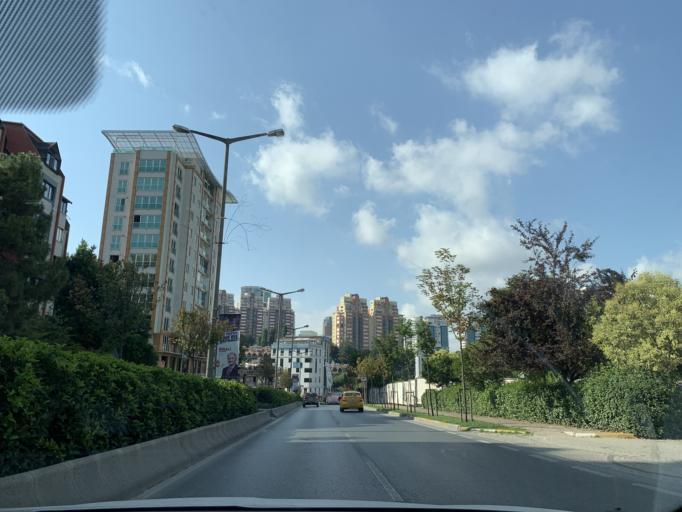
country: TR
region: Istanbul
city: Esenyurt
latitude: 41.0680
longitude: 28.6843
